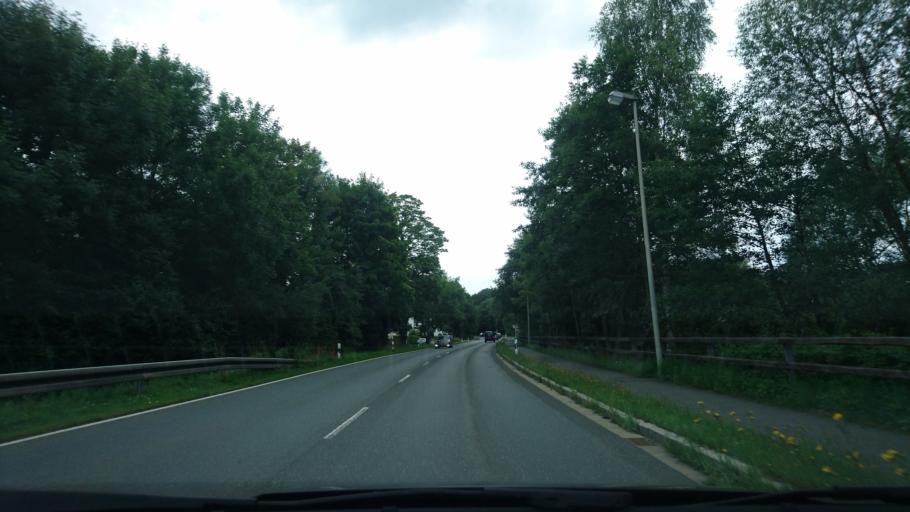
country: DE
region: Bavaria
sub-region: Upper Franconia
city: Naila
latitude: 50.3546
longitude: 11.6932
